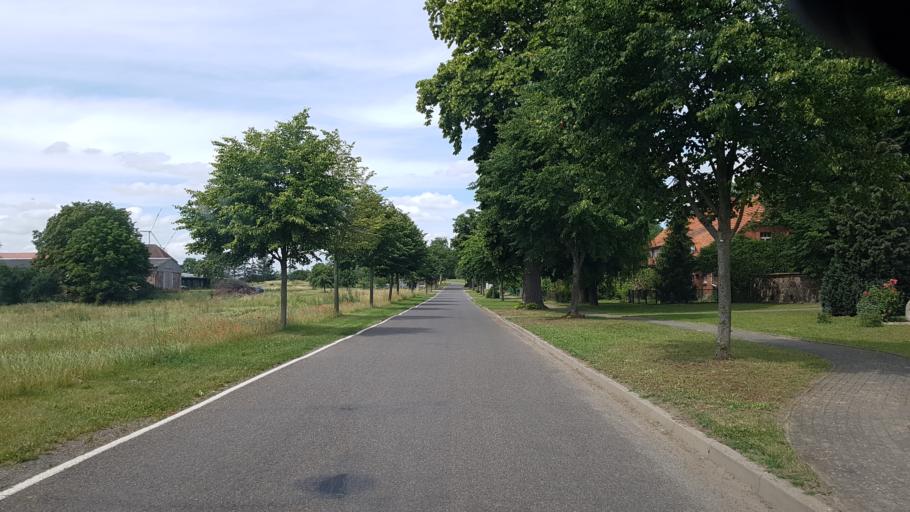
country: DE
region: Mecklenburg-Vorpommern
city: Strasburg
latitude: 53.4433
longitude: 13.7713
